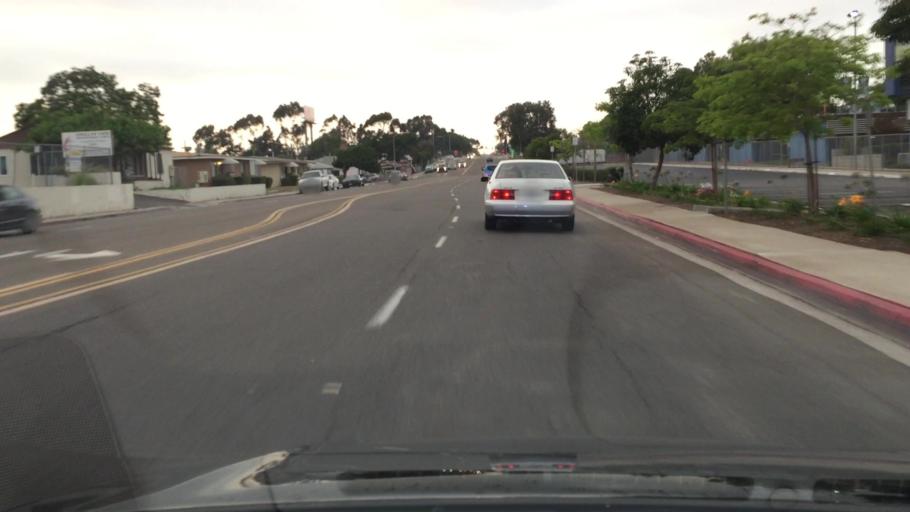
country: US
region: California
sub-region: San Diego County
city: National City
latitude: 32.7153
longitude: -117.0935
